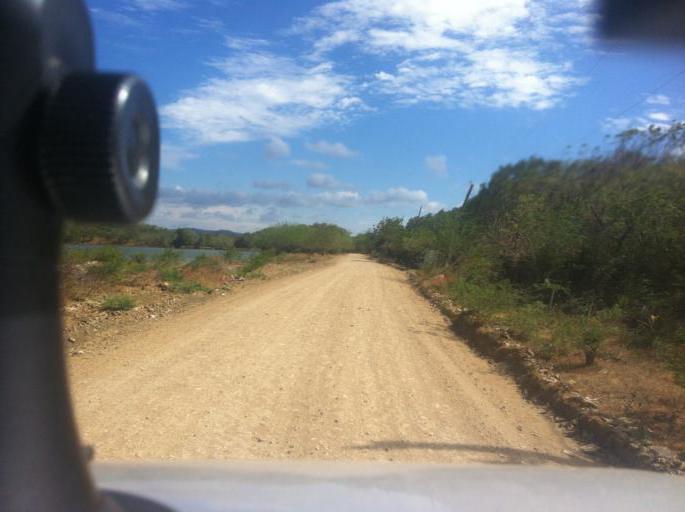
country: NI
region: Rivas
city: Tola
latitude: 11.4764
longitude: -86.1045
